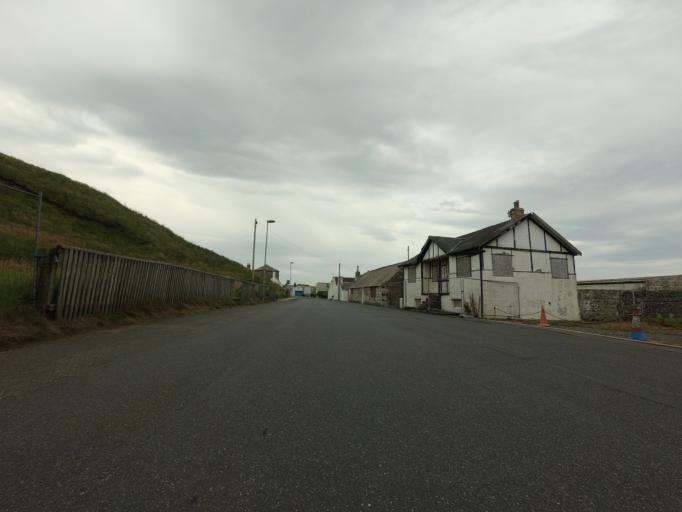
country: GB
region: Scotland
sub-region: Aberdeenshire
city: Whitehills
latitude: 57.6794
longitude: -2.5787
